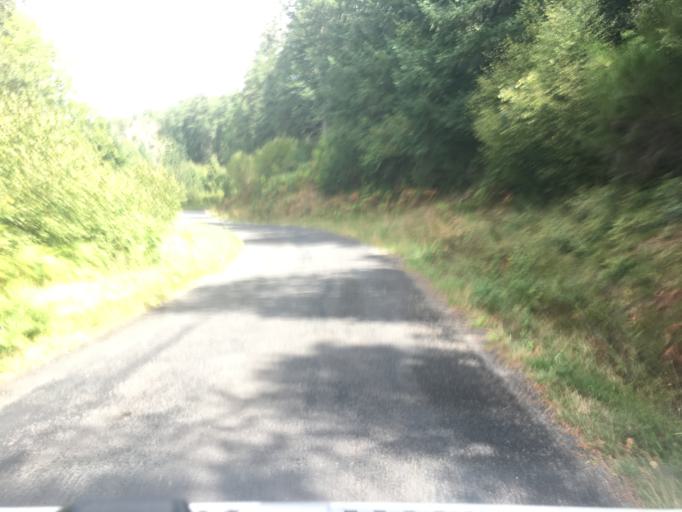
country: FR
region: Auvergne
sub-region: Departement du Cantal
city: Champagnac
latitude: 45.4367
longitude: 2.4053
